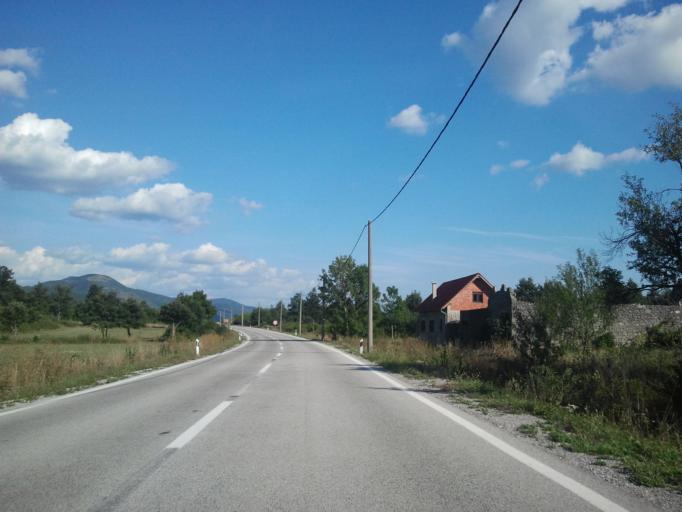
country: HR
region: Zadarska
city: Obrovac
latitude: 44.3756
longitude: 15.6584
